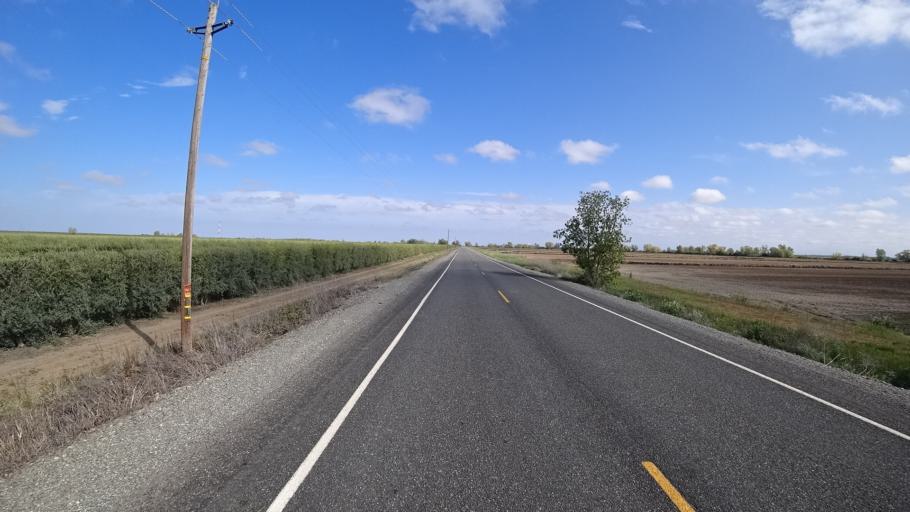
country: US
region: California
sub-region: Butte County
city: Durham
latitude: 39.4689
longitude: -121.9301
